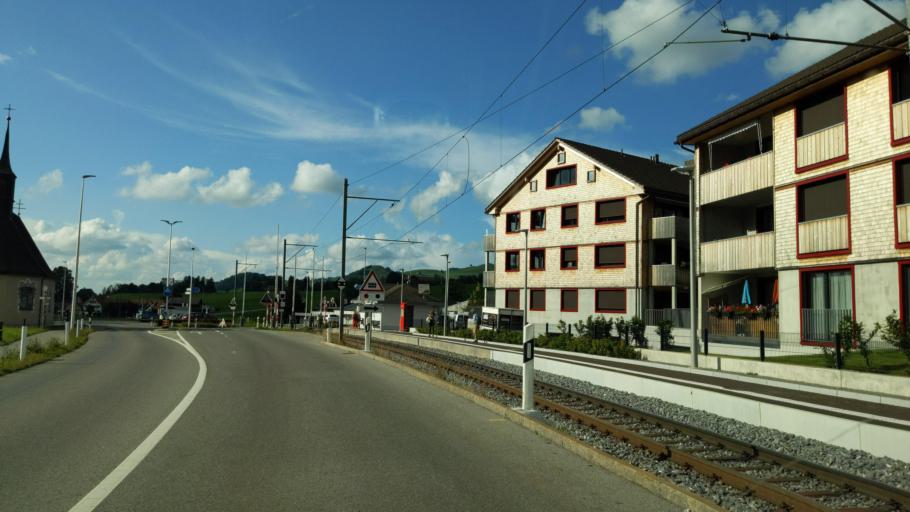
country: CH
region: Appenzell Innerrhoden
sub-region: Appenzell Inner Rhodes
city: Appenzell
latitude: 47.3201
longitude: 9.4307
